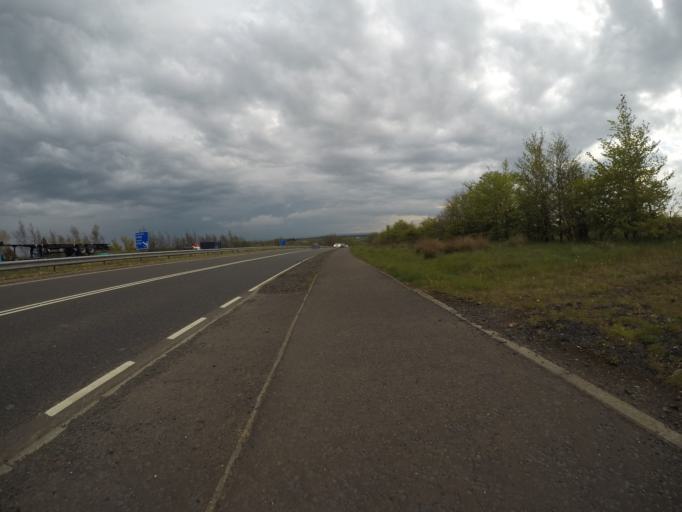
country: GB
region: Scotland
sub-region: East Ayrshire
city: Kilmarnock
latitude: 55.6596
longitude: -4.4481
